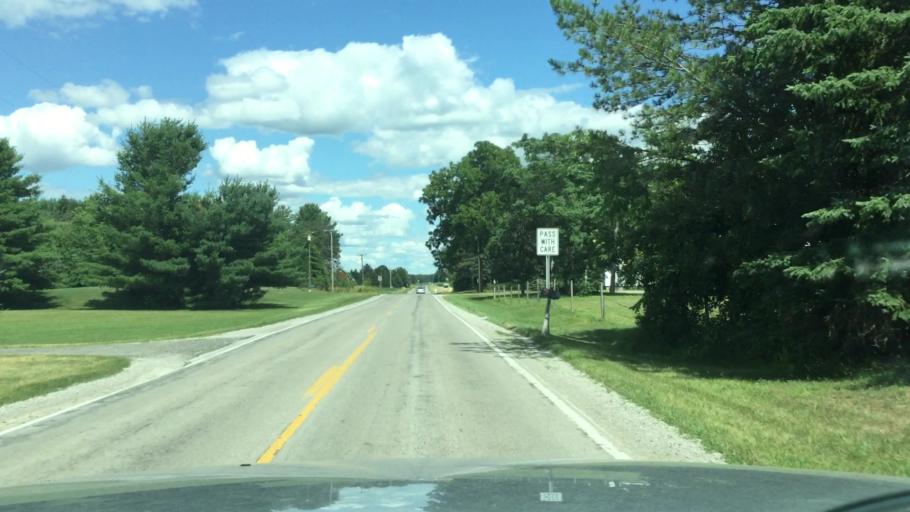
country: US
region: Michigan
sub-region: Saginaw County
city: Hemlock
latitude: 43.3787
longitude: -84.1830
